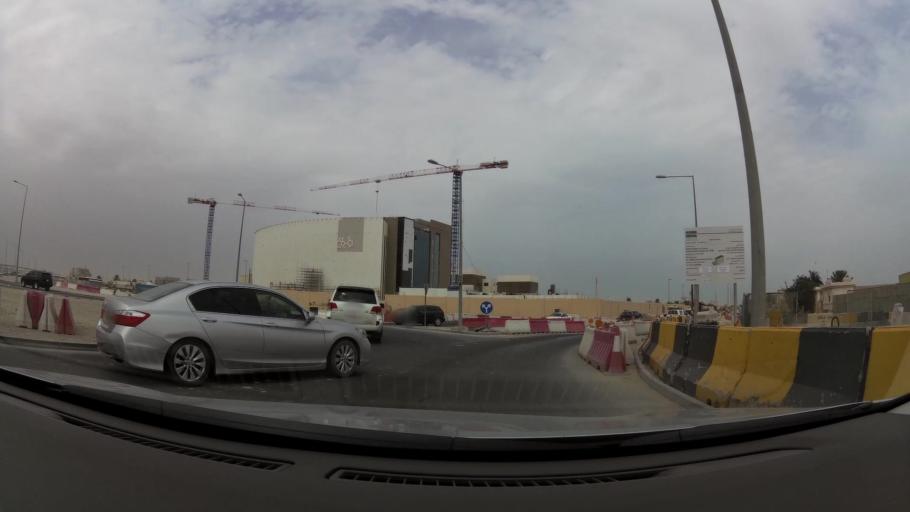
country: QA
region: Baladiyat ar Rayyan
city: Ar Rayyan
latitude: 25.3515
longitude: 51.4551
